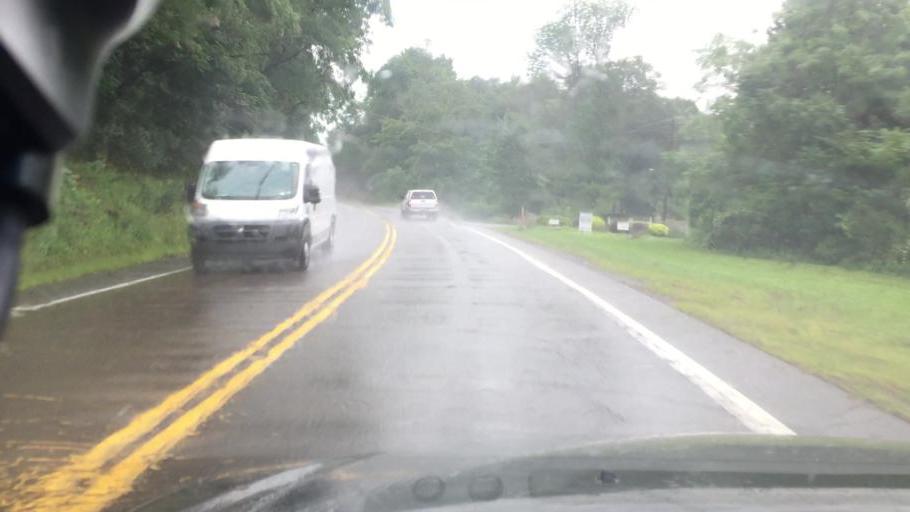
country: US
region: Pennsylvania
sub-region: Luzerne County
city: White Haven
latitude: 41.0496
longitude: -75.7766
